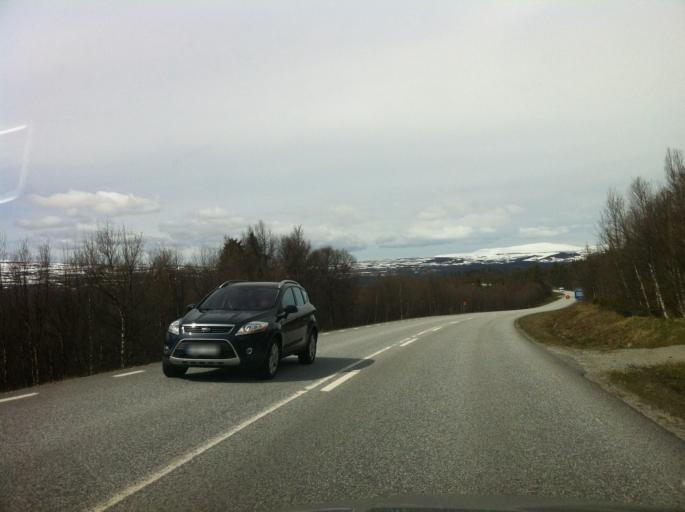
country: NO
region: Hedmark
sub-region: Engerdal
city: Engerdal
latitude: 62.5376
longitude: 12.4256
